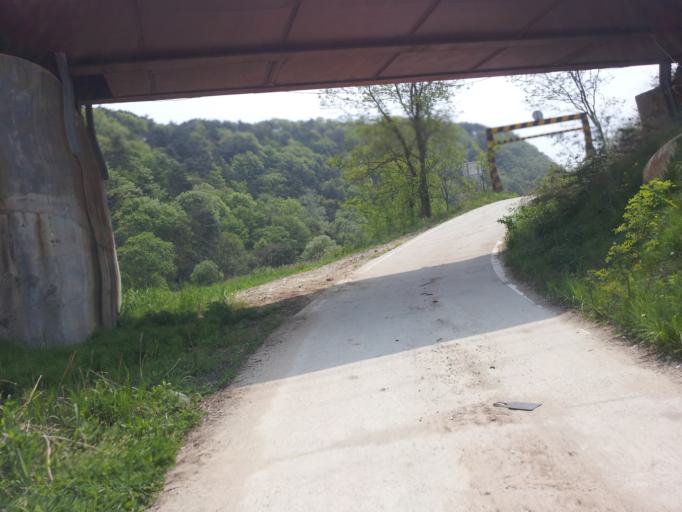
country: KR
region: Daejeon
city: Daejeon
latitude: 36.2641
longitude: 127.2912
